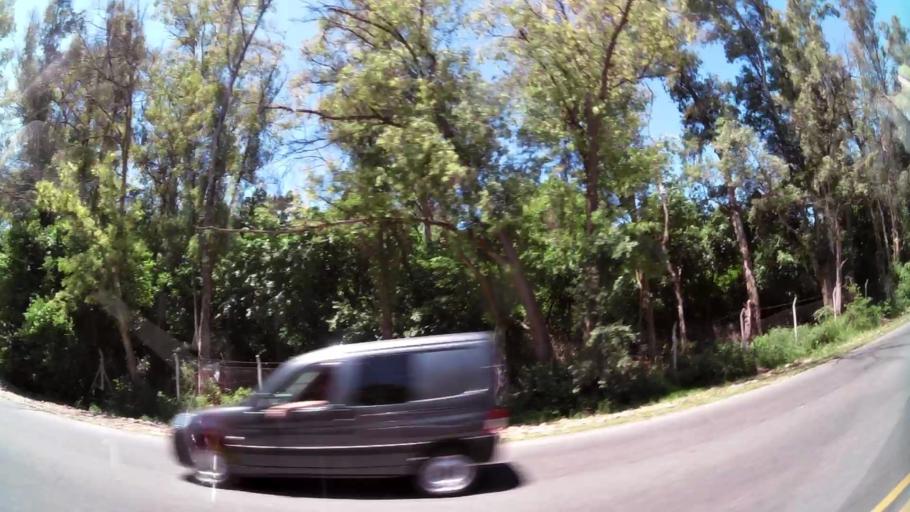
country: AR
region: Buenos Aires
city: Hurlingham
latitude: -34.5213
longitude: -58.6759
